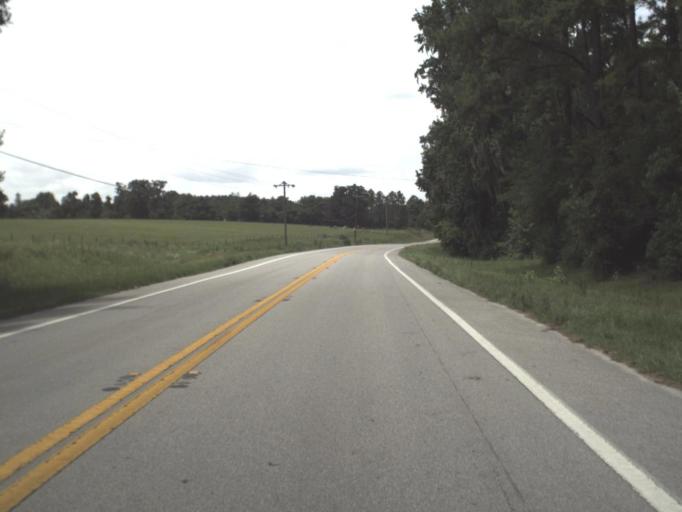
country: US
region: Florida
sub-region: Madison County
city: Madison
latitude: 30.5888
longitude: -83.4301
